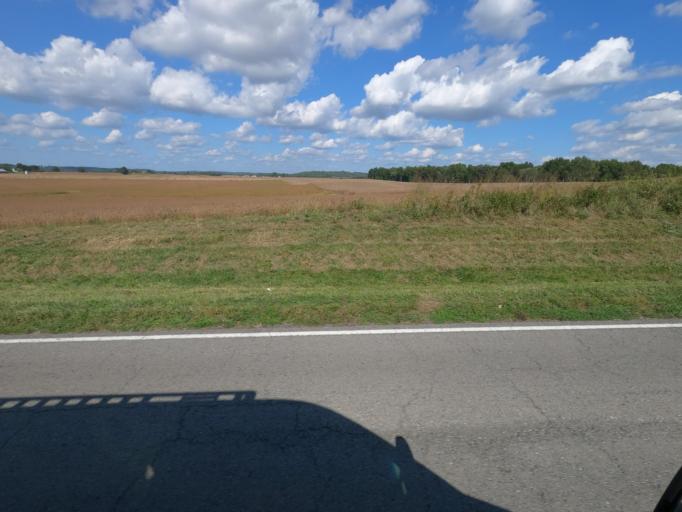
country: US
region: Illinois
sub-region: Massac County
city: Metropolis
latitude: 37.2598
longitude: -88.7551
